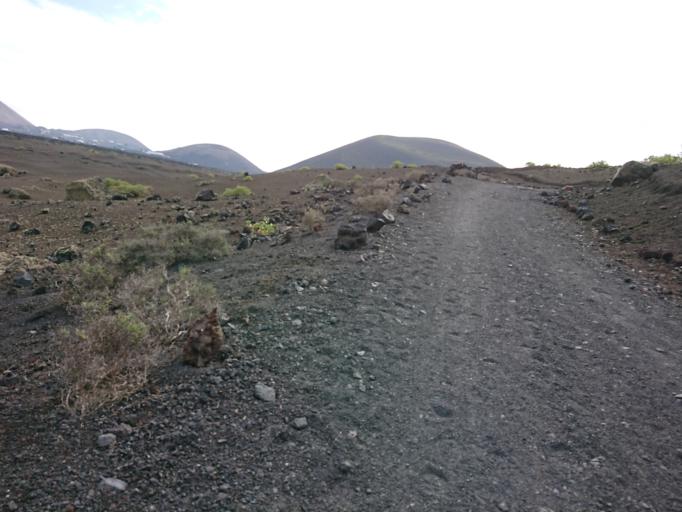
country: ES
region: Canary Islands
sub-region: Provincia de Las Palmas
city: Tias
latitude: 29.0059
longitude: -13.6757
